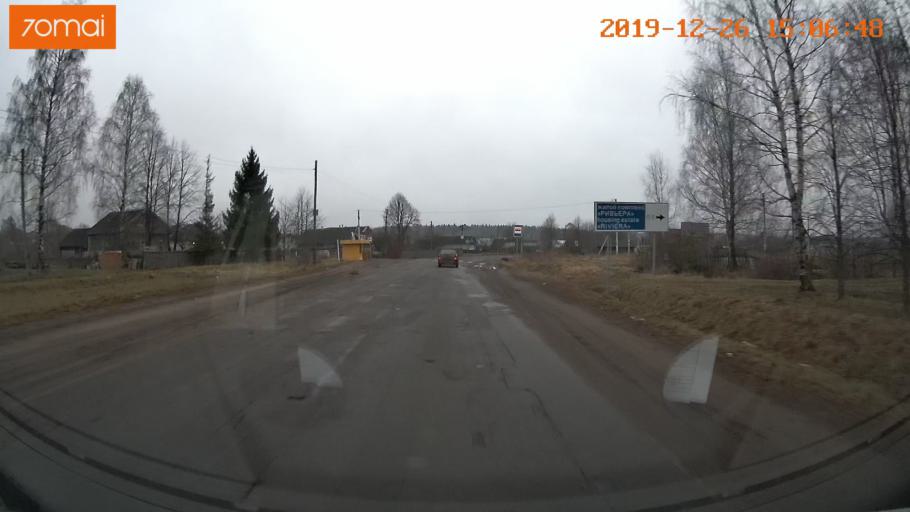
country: RU
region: Jaroslavl
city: Rybinsk
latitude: 58.1749
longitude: 38.8435
